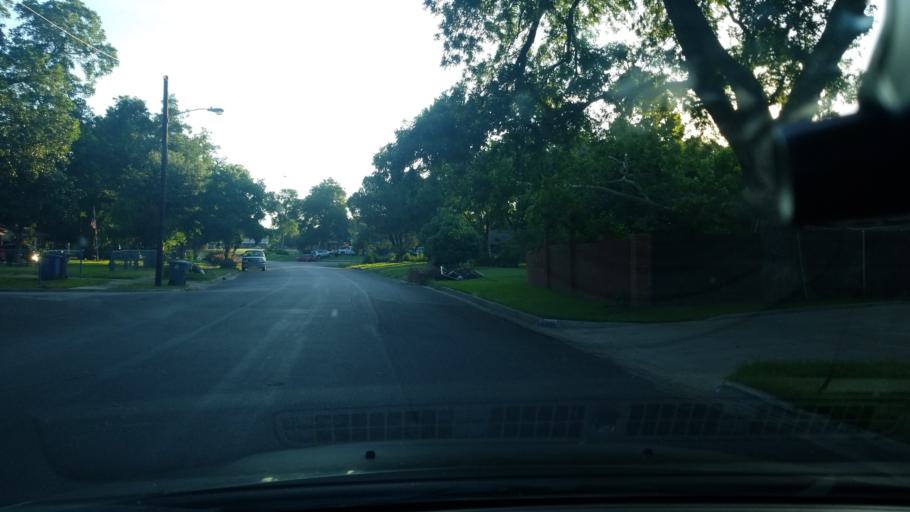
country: US
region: Texas
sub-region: Dallas County
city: Cockrell Hill
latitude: 32.7162
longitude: -96.8318
